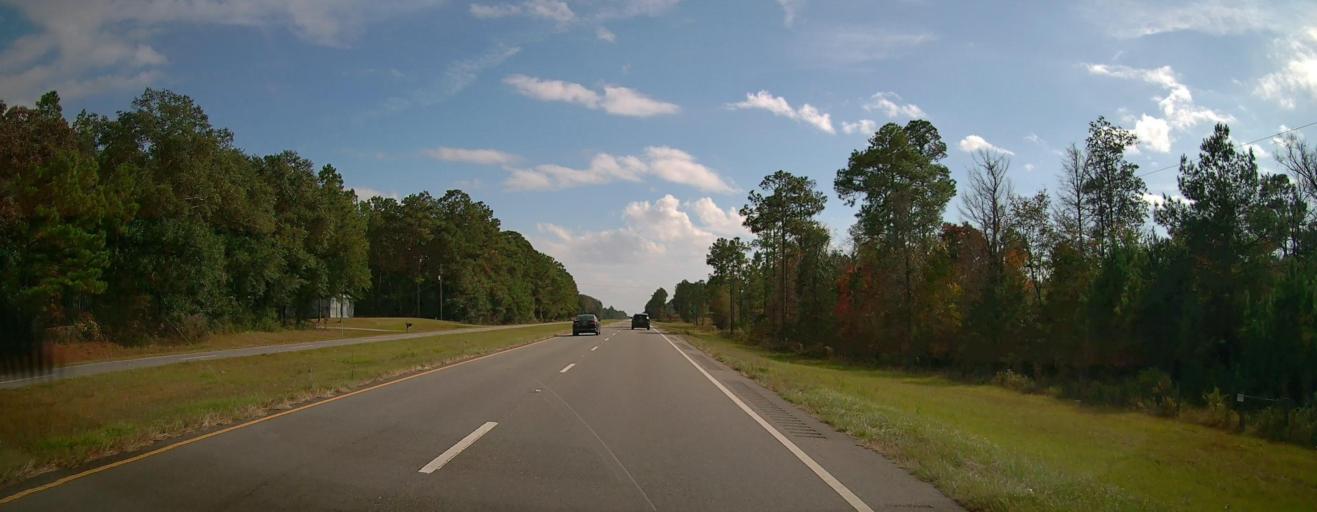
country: US
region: Georgia
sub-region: Thomas County
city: Meigs
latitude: 30.9683
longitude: -84.0330
